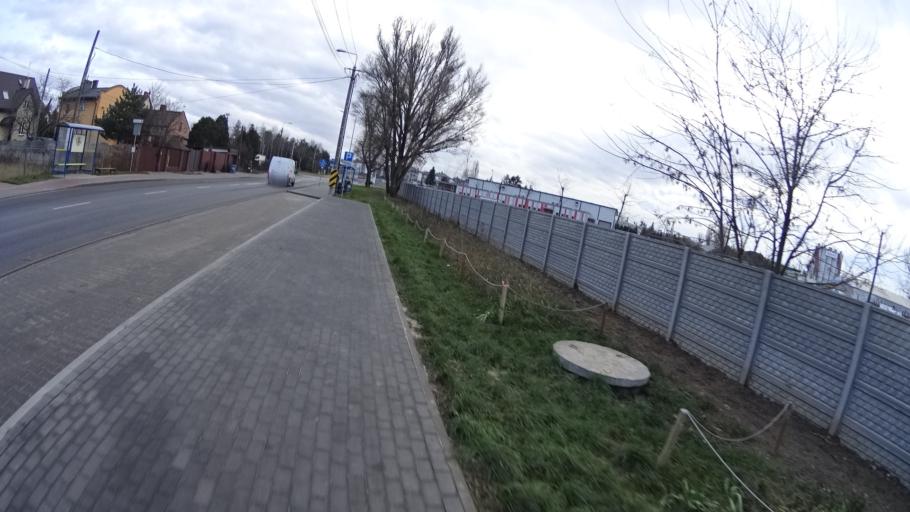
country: PL
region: Masovian Voivodeship
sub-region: Powiat pruszkowski
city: Pruszkow
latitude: 52.1646
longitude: 20.7784
